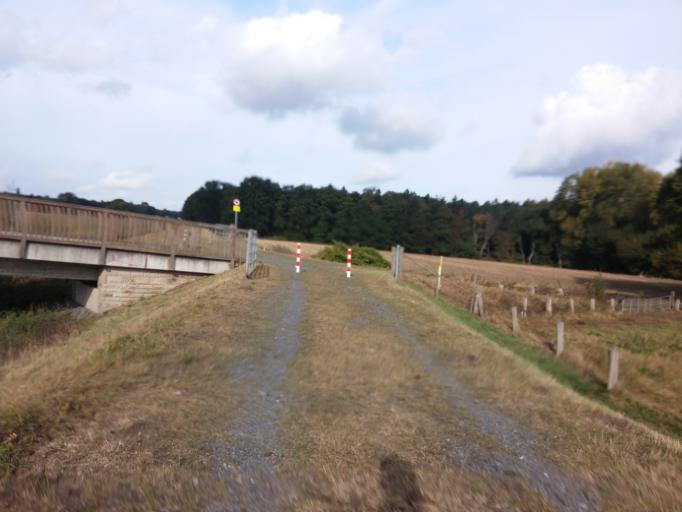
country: DE
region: North Rhine-Westphalia
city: Dorsten
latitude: 51.6500
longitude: 6.9983
